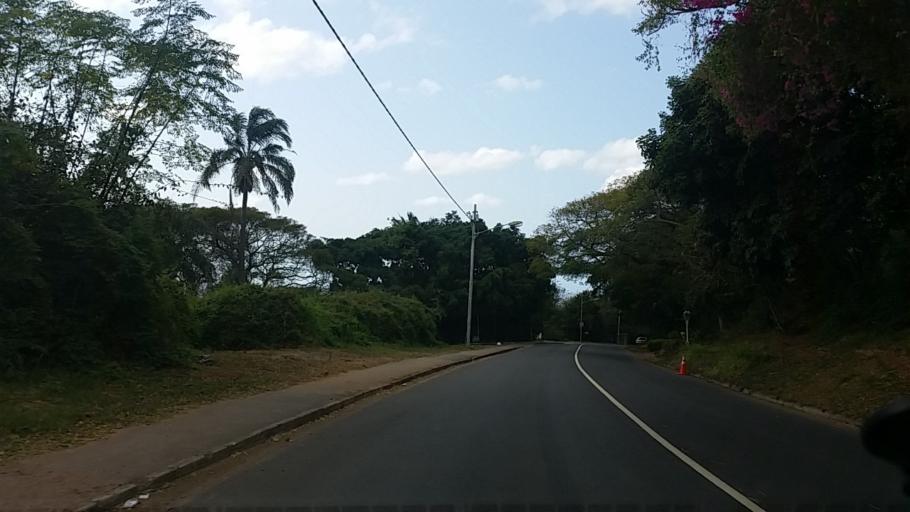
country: ZA
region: KwaZulu-Natal
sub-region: eThekwini Metropolitan Municipality
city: Berea
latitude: -29.8299
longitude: 30.9371
